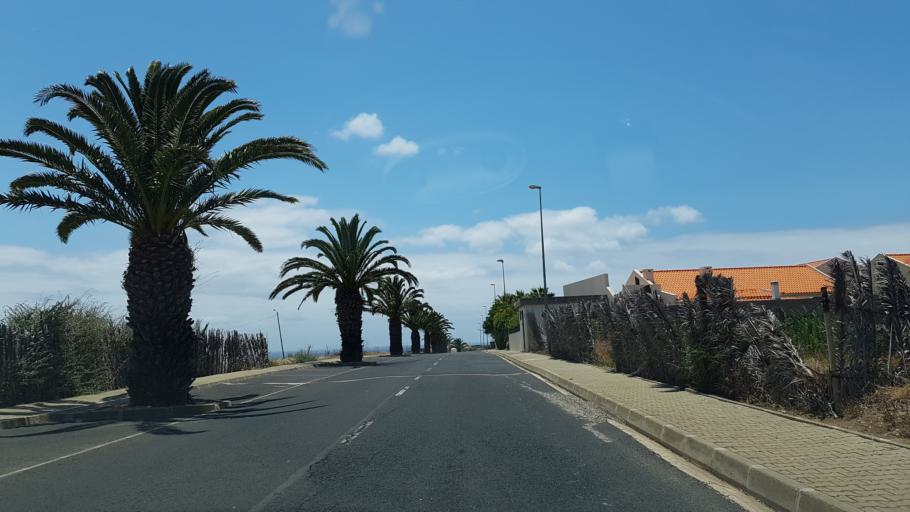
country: PT
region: Madeira
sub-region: Porto Santo
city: Vila de Porto Santo
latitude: 33.0657
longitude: -16.3437
